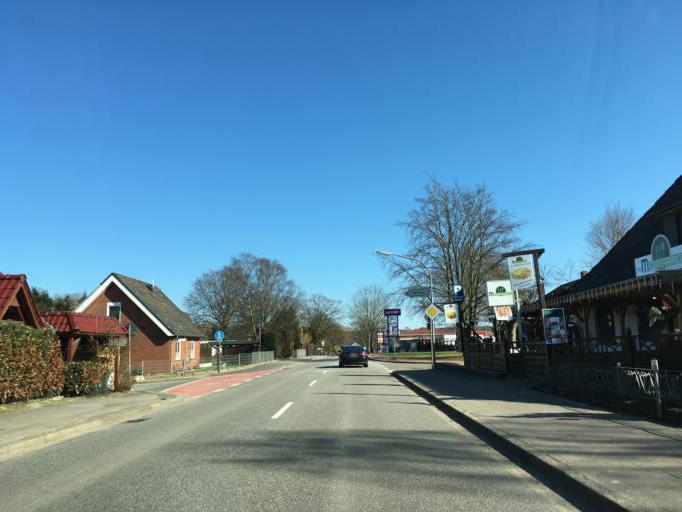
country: DE
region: Schleswig-Holstein
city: Berkenthin
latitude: 53.7346
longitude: 10.6409
